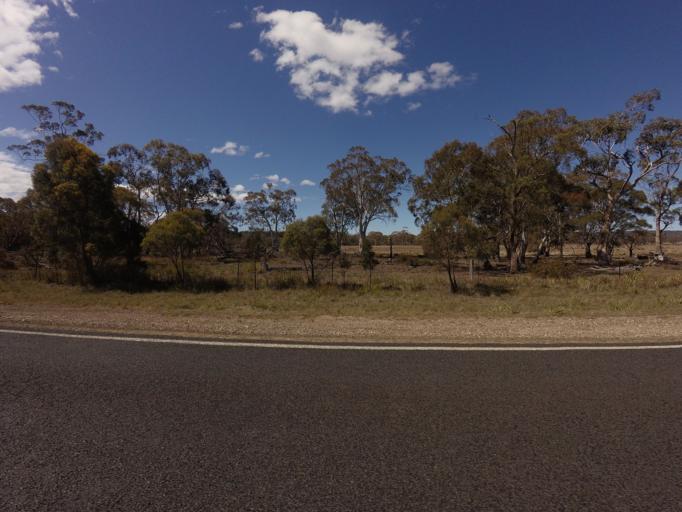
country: AU
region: Tasmania
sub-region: Break O'Day
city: St Helens
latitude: -42.0393
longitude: 148.0287
